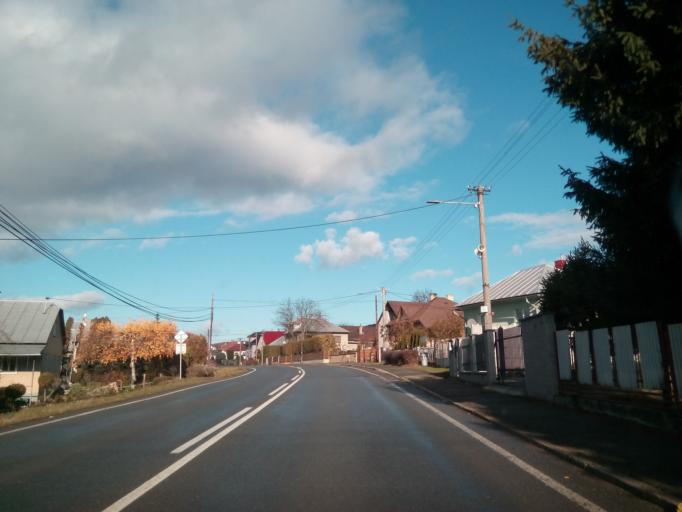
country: SK
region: Presovsky
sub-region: Okres Bardejov
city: Bardejov
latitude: 49.2160
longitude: 21.2959
